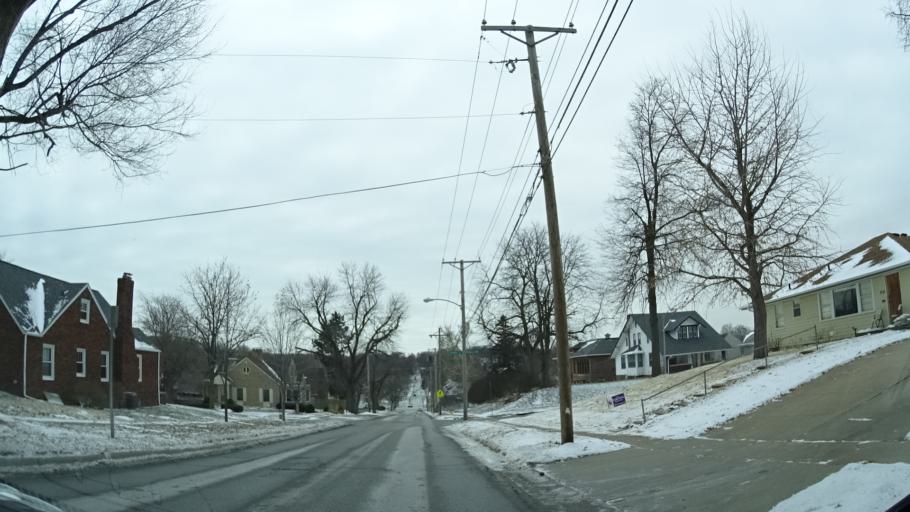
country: US
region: Nebraska
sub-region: Douglas County
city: Omaha
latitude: 41.2435
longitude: -95.9855
